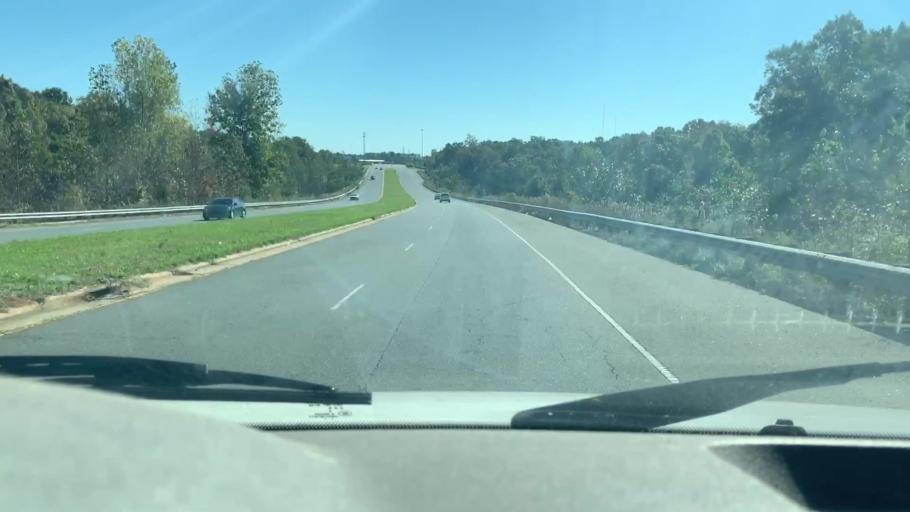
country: US
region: North Carolina
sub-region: Mecklenburg County
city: Charlotte
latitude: 35.2936
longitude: -80.7765
